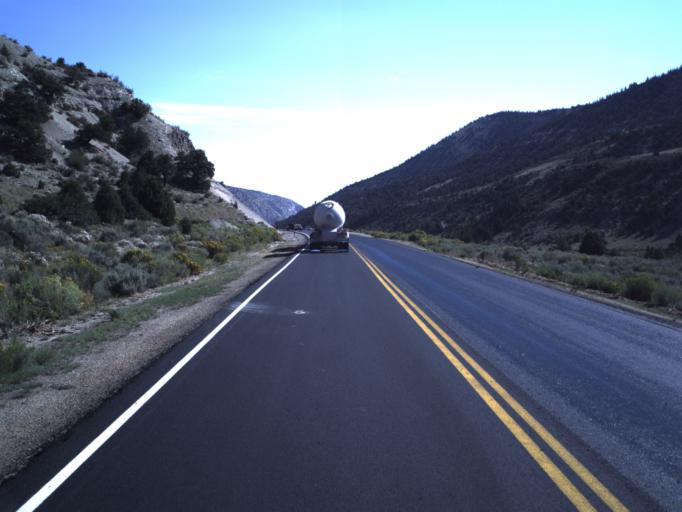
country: US
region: Utah
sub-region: Carbon County
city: Helper
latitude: 39.9323
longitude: -110.6735
